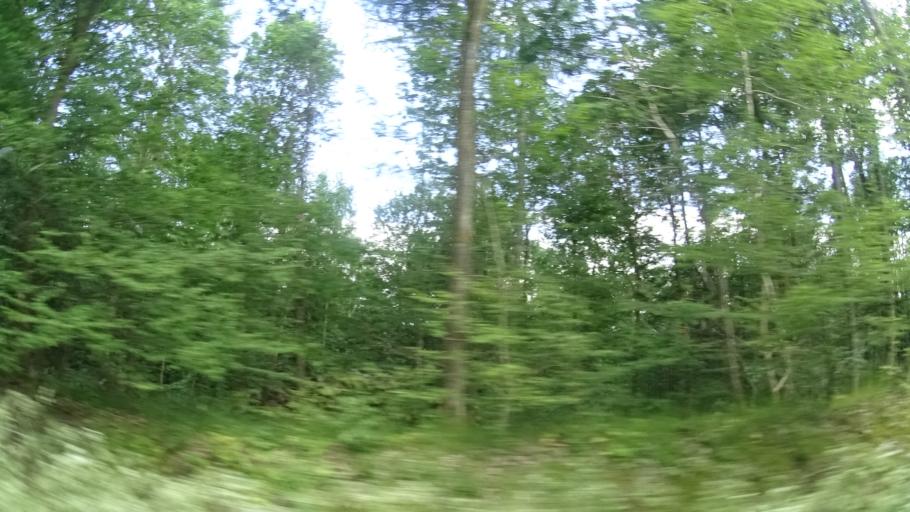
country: DE
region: Hesse
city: Haina
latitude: 51.0395
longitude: 8.9783
